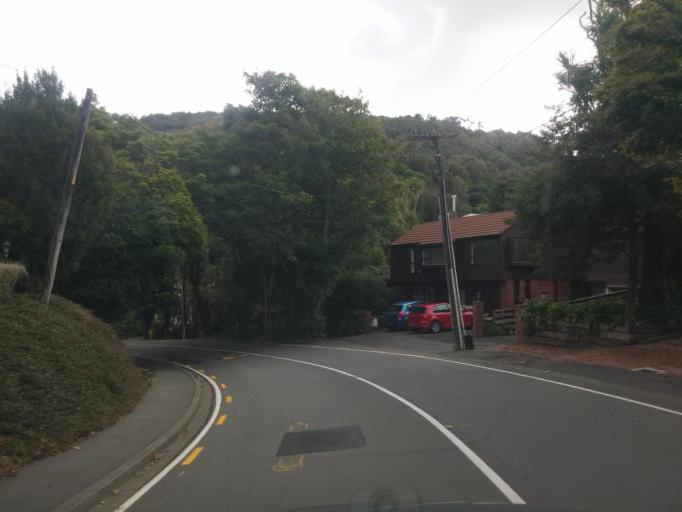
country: NZ
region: Wellington
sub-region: Wellington City
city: Wellington
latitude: -41.2455
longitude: 174.7863
